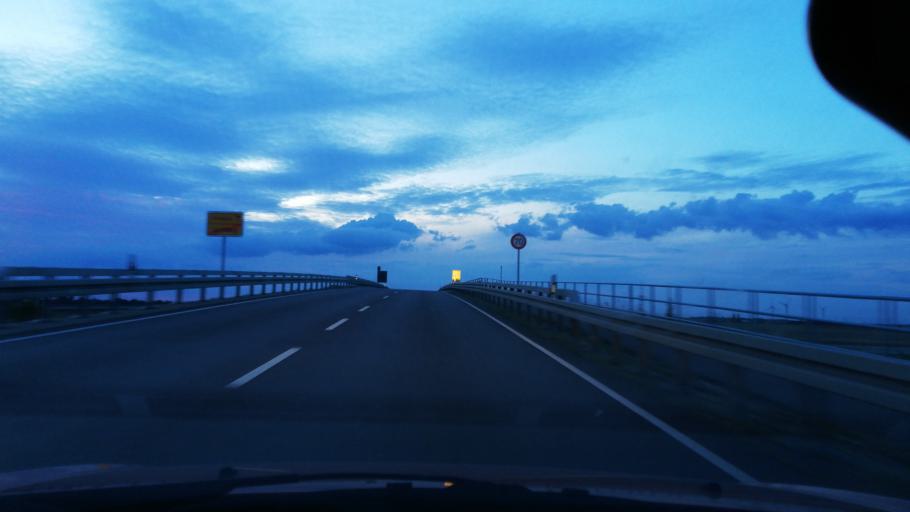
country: DE
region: Saxony-Anhalt
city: Landsberg
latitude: 51.5398
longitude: 12.1564
